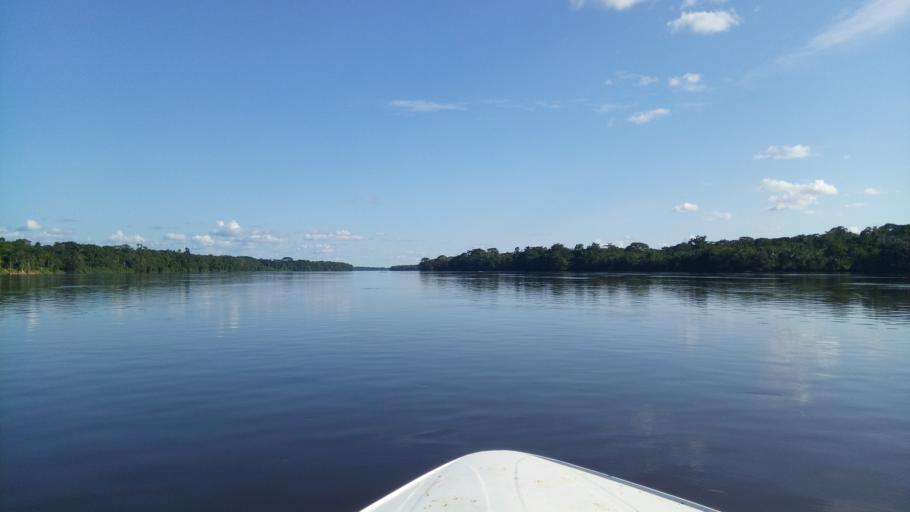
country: CD
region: Eastern Province
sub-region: Sous-Region de la Tshopo
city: Yangambi
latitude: 0.4456
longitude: 24.1632
